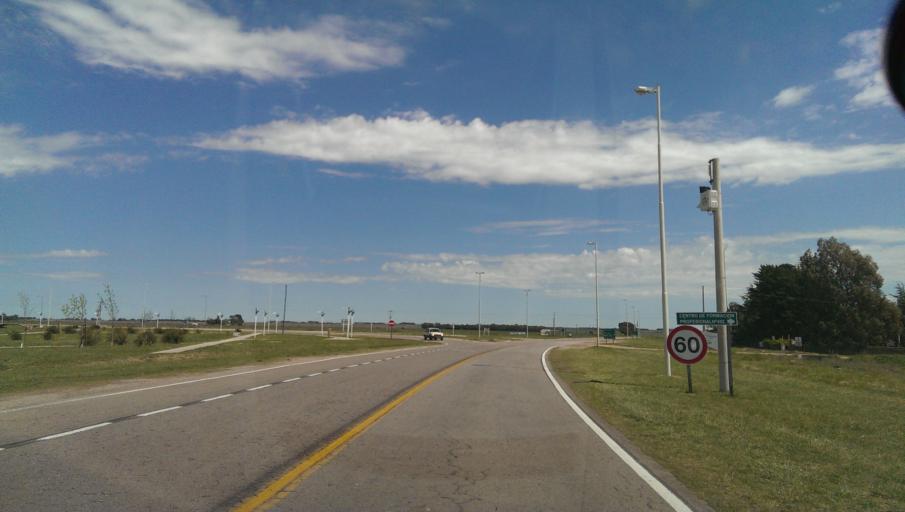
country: AR
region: Buenos Aires
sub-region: Partido de Tornquist
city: Tornquist
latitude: -38.0699
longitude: -62.2198
